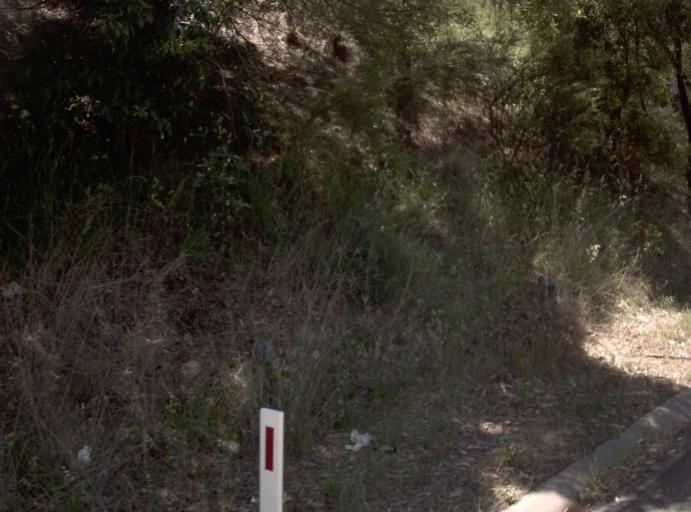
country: AU
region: Victoria
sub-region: East Gippsland
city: Lakes Entrance
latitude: -37.8496
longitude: 148.0386
